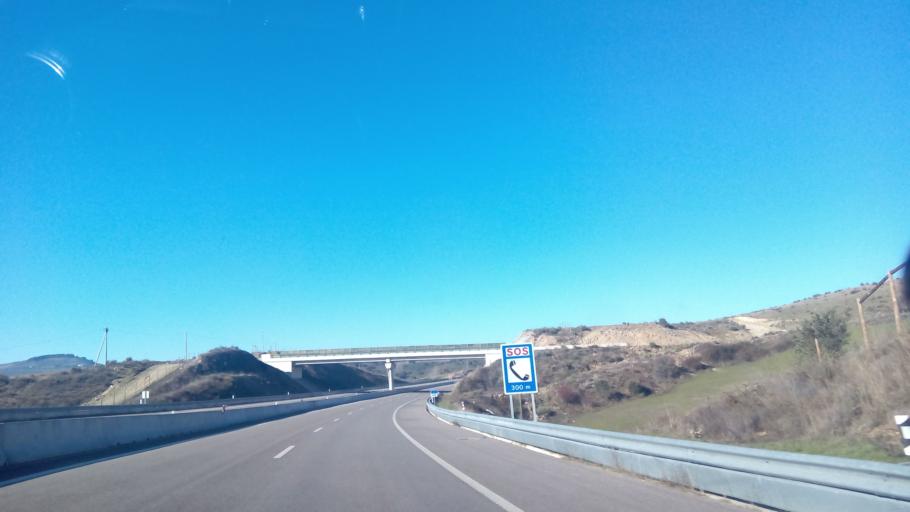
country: PT
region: Braganca
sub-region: Braganca Municipality
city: Braganca
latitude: 41.7826
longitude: -6.7044
